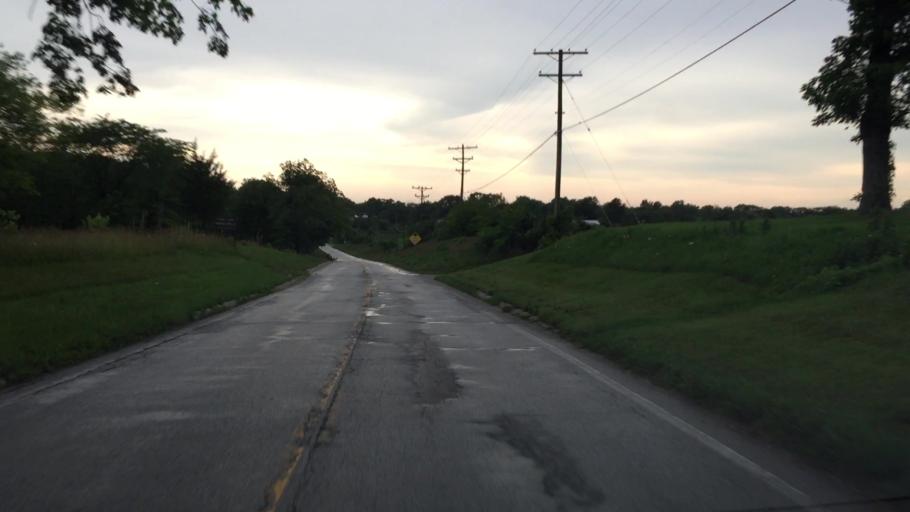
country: US
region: Illinois
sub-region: Hancock County
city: Warsaw
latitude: 40.3562
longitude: -91.4117
